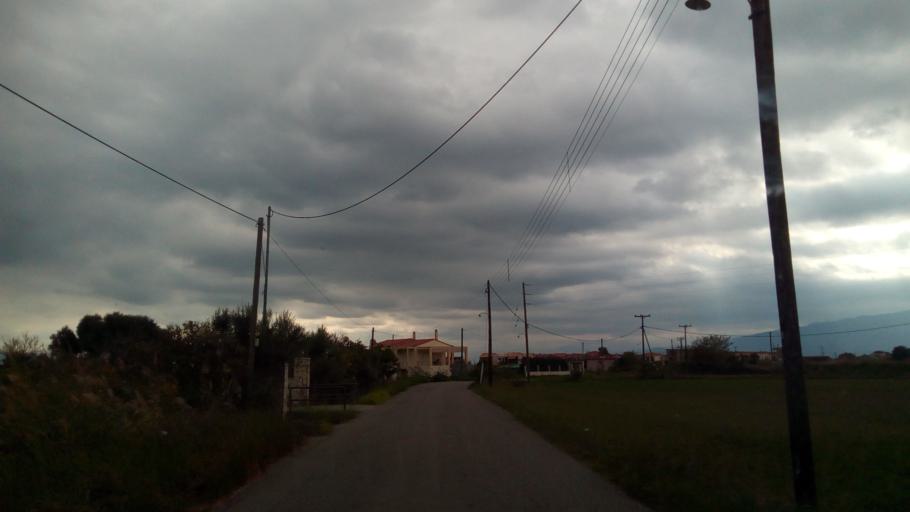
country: GR
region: West Greece
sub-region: Nomos Aitolias kai Akarnanias
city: Nafpaktos
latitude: 38.3952
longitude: 21.9154
